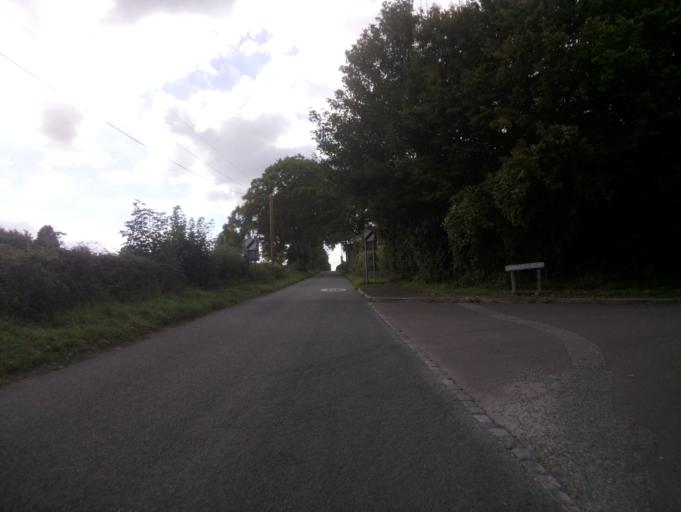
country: GB
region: England
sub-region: Wiltshire
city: Salisbury
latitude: 51.0946
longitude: -1.7807
